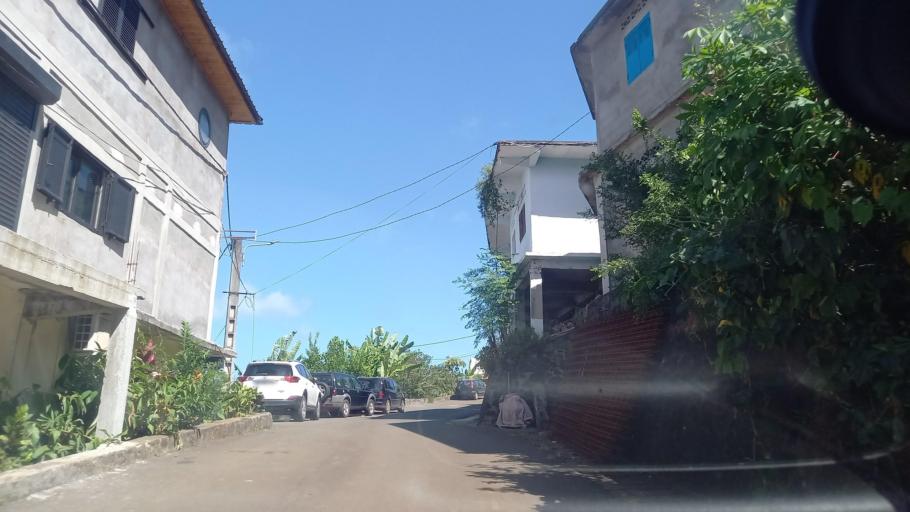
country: YT
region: Chiconi
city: Chiconi
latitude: -12.8352
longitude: 45.1122
